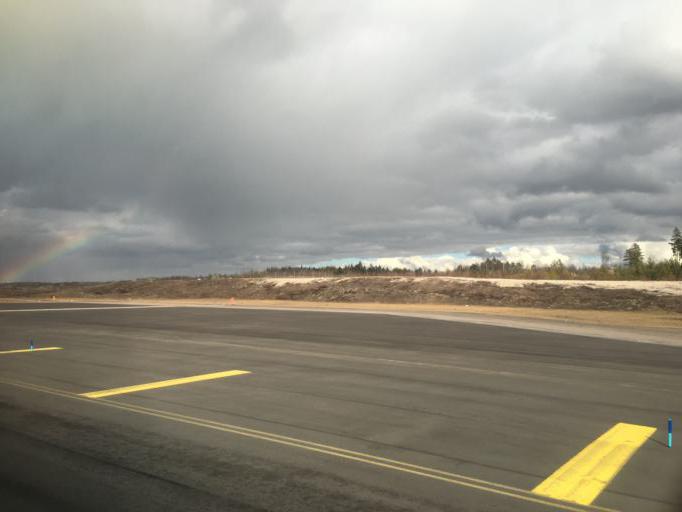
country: SE
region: Stockholm
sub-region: Sigtuna Kommun
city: Marsta
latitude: 59.6649
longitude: 17.9264
